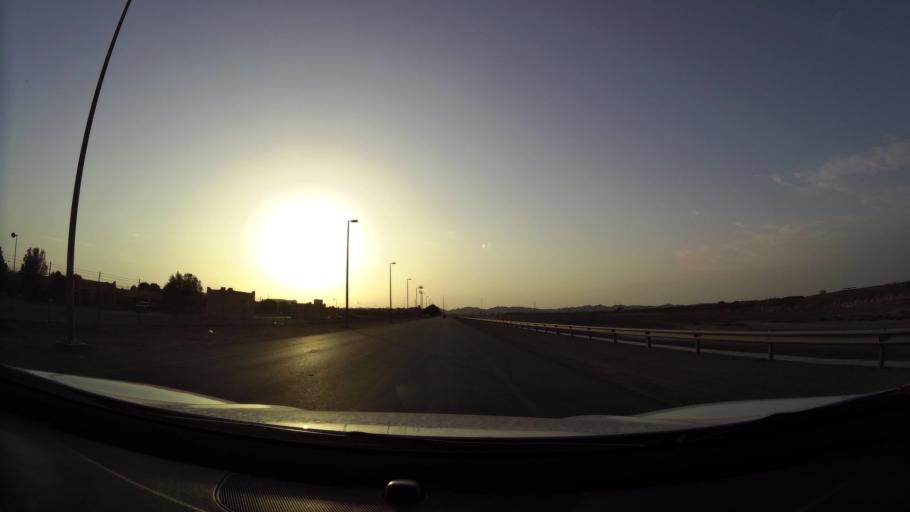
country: AE
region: Abu Dhabi
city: Al Ain
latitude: 24.1643
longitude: 55.8155
